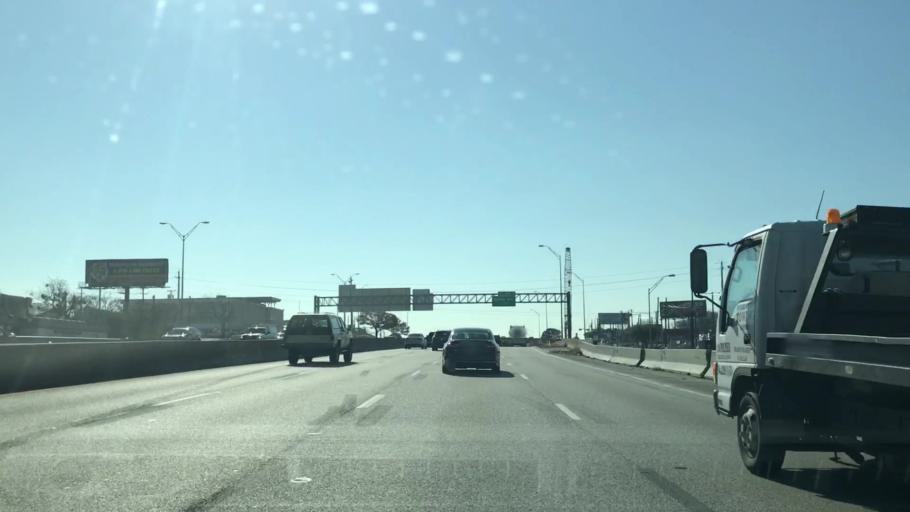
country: US
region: Texas
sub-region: Dallas County
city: Dallas
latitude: 32.7545
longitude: -96.8096
